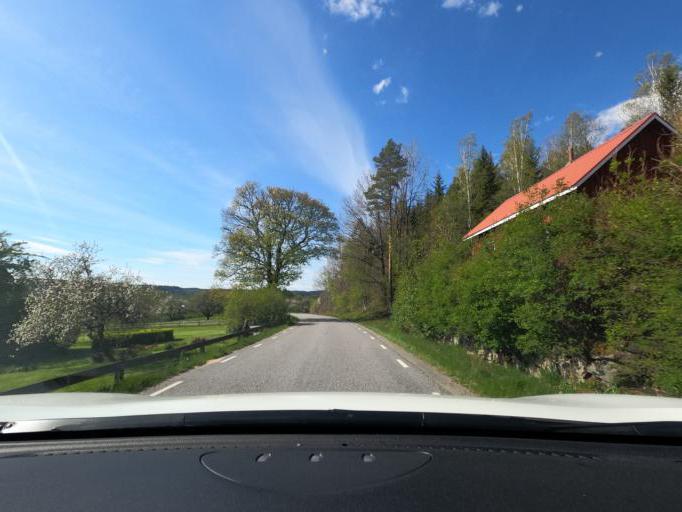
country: SE
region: Vaestra Goetaland
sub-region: Harryda Kommun
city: Ravlanda
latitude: 57.6362
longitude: 12.4980
